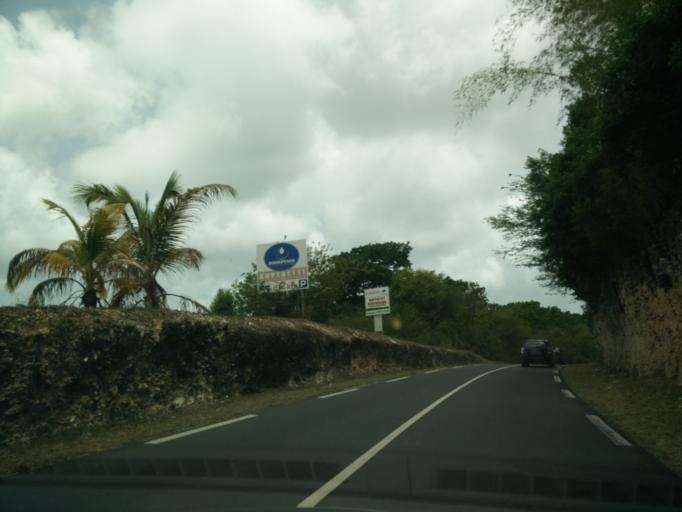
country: GP
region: Guadeloupe
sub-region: Guadeloupe
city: Petit-Canal
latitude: 16.3715
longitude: -61.4678
